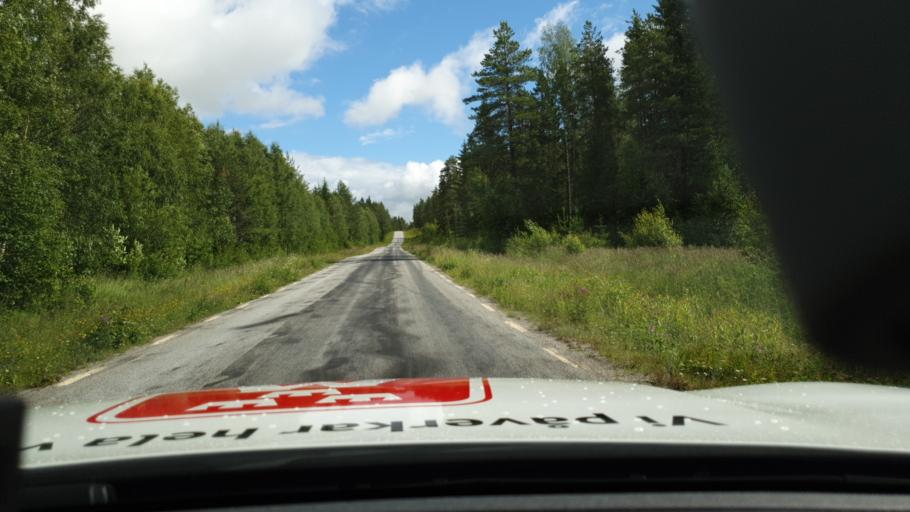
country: SE
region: Norrbotten
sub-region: Pitea Kommun
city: Rosvik
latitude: 65.4140
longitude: 21.7690
